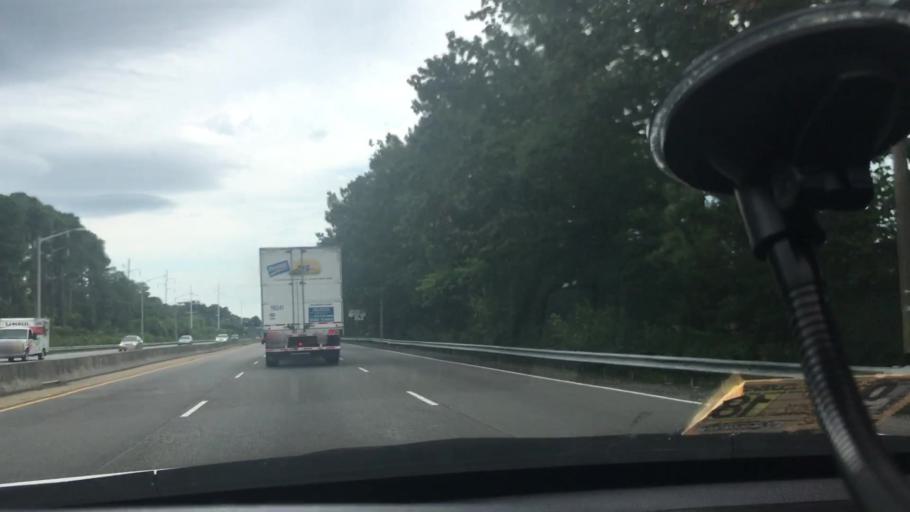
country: US
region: Virginia
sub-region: City of Norfolk
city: Norfolk
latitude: 36.8958
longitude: -76.1513
